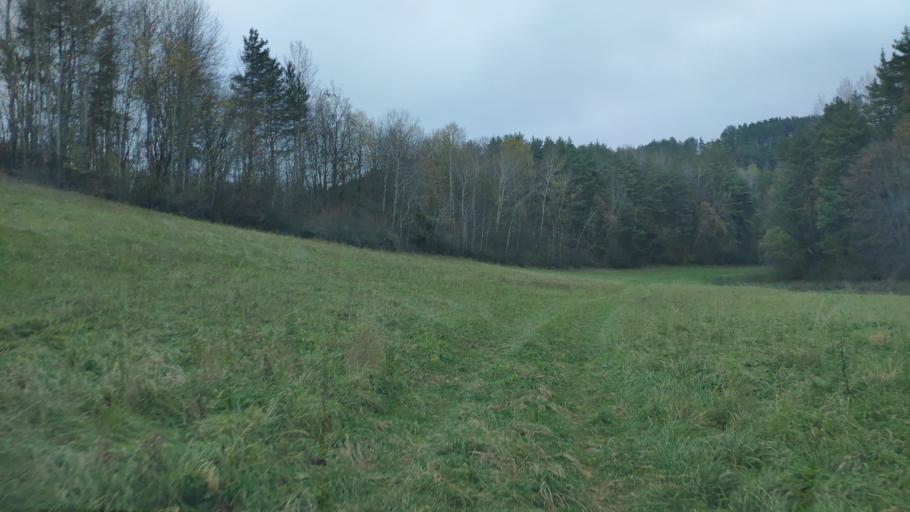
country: SK
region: Presovsky
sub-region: Okres Presov
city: Presov
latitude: 48.9296
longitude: 21.1010
